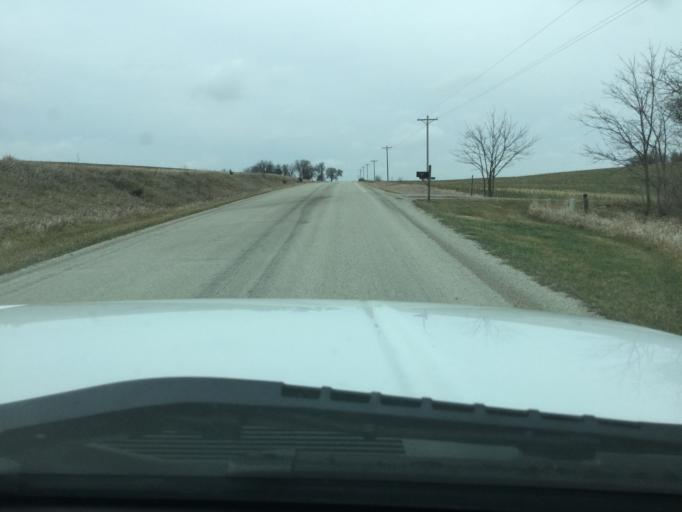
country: US
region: Kansas
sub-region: Nemaha County
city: Sabetha
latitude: 39.8895
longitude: -95.7139
